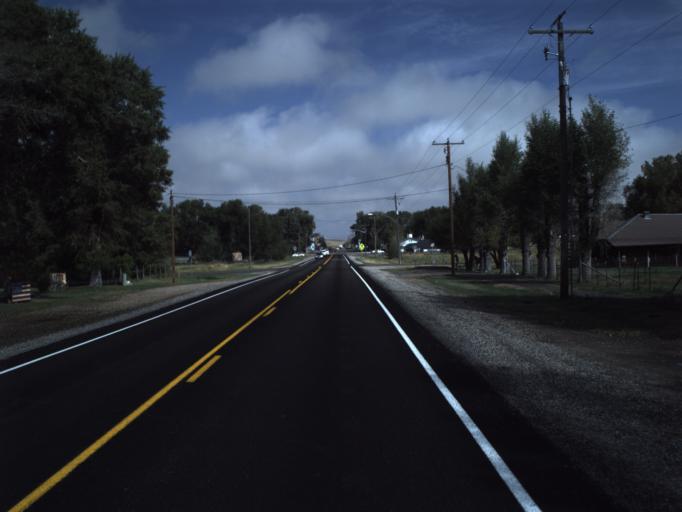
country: US
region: Utah
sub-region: Rich County
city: Randolph
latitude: 41.6603
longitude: -111.1849
